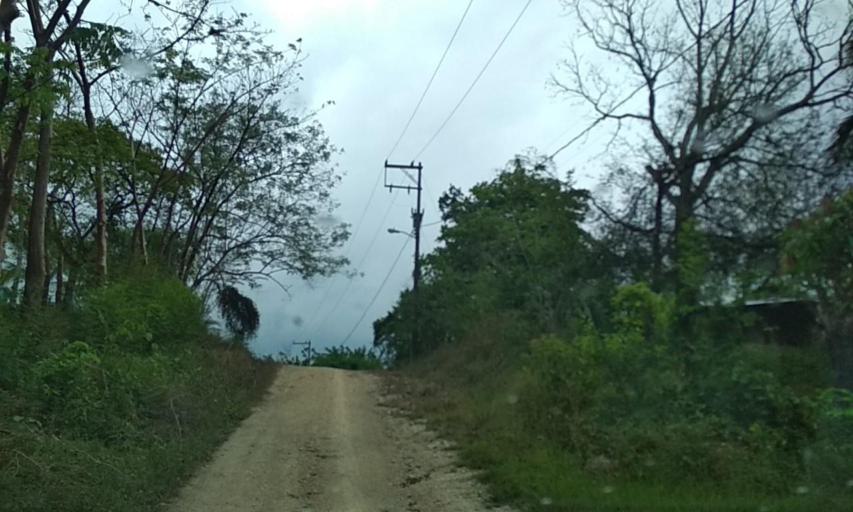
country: MX
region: Tabasco
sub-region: Huimanguillo
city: Francisco Rueda
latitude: 17.6560
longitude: -94.0989
